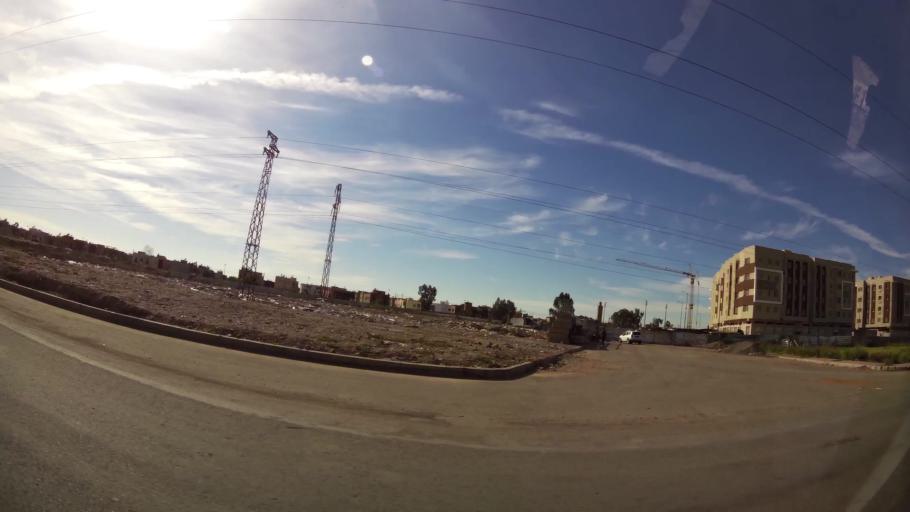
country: MA
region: Marrakech-Tensift-Al Haouz
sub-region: Marrakech
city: Marrakesh
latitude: 31.6463
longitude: -8.0382
